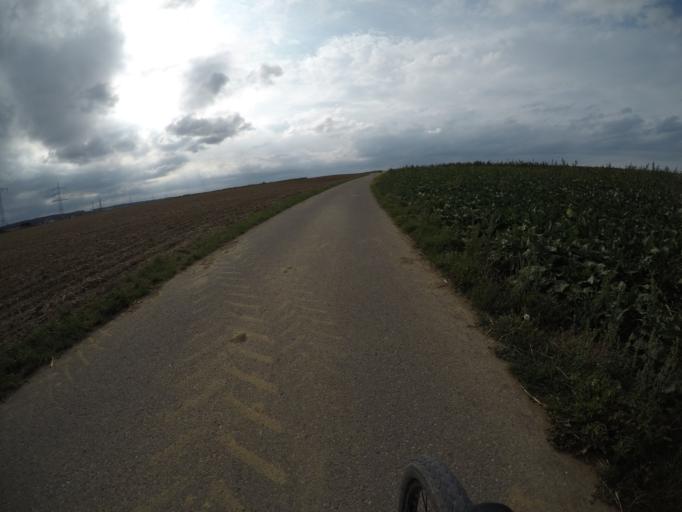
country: DE
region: Baden-Wuerttemberg
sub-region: Regierungsbezirk Stuttgart
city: Herrenberg
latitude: 48.6251
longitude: 8.8589
